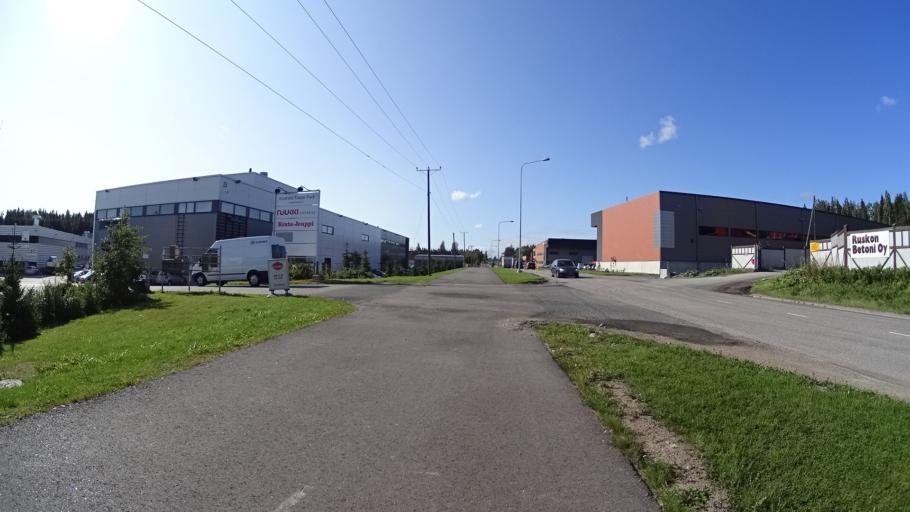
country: FI
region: Uusimaa
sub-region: Helsinki
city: Kauniainen
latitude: 60.2622
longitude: 24.7224
